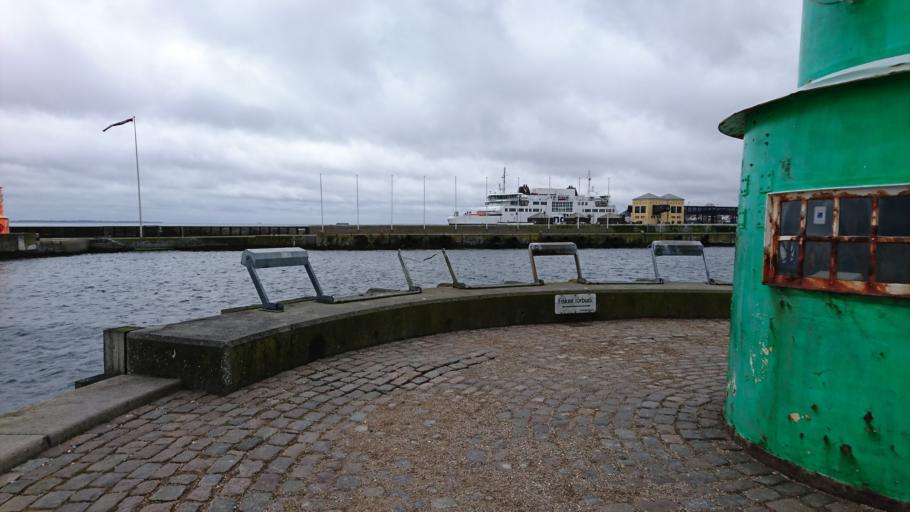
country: DK
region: Capital Region
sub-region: Helsingor Kommune
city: Helsingor
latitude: 56.0350
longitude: 12.6195
